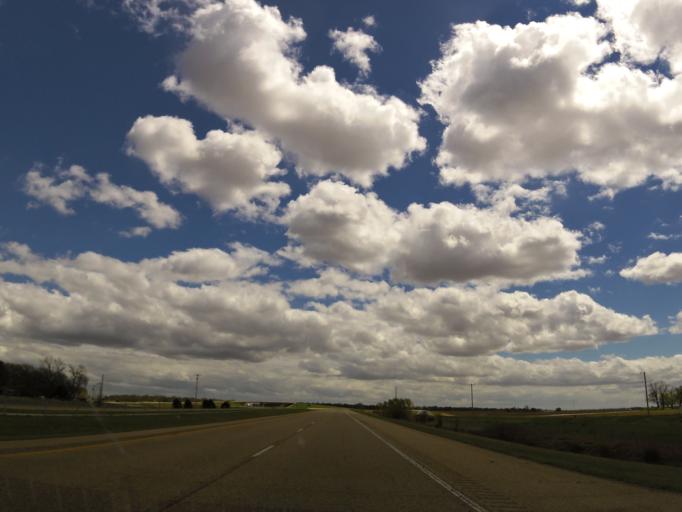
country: US
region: Arkansas
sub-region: Poinsett County
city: Marked Tree
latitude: 35.4843
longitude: -90.3642
